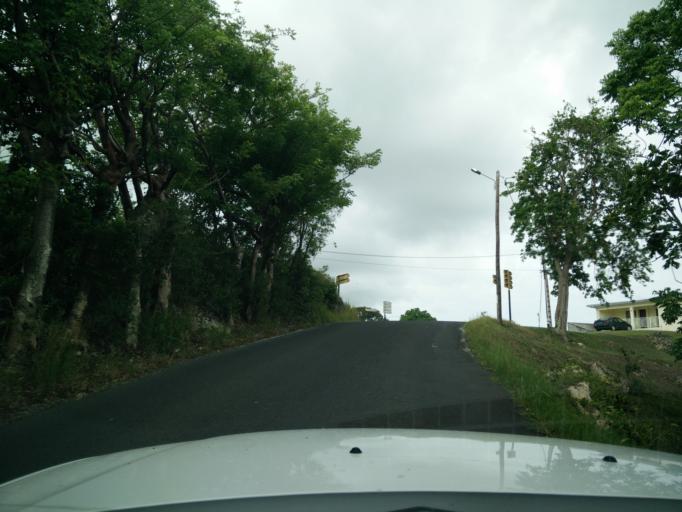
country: GP
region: Guadeloupe
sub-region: Guadeloupe
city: Le Gosier
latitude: 16.2403
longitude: -61.4484
